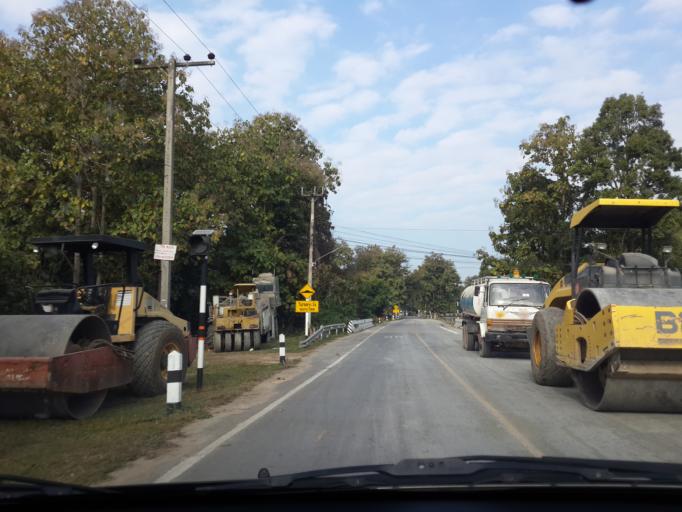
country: TH
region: Chiang Mai
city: San Sai
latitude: 18.9029
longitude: 99.0178
